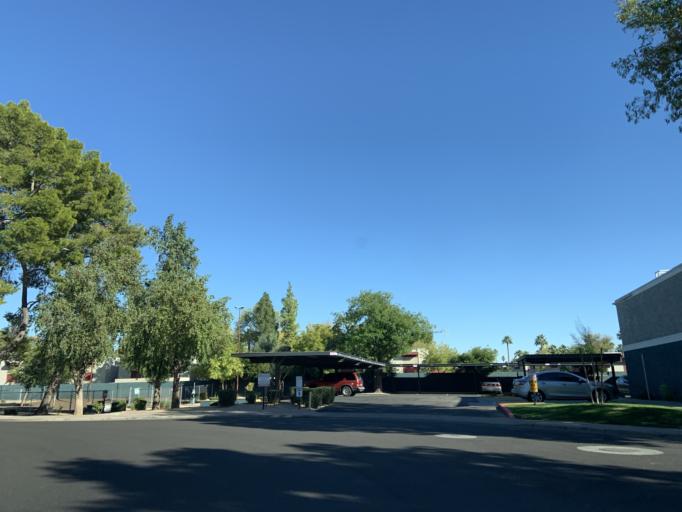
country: US
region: Arizona
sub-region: Maricopa County
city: Tempe
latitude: 33.3959
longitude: -111.8775
